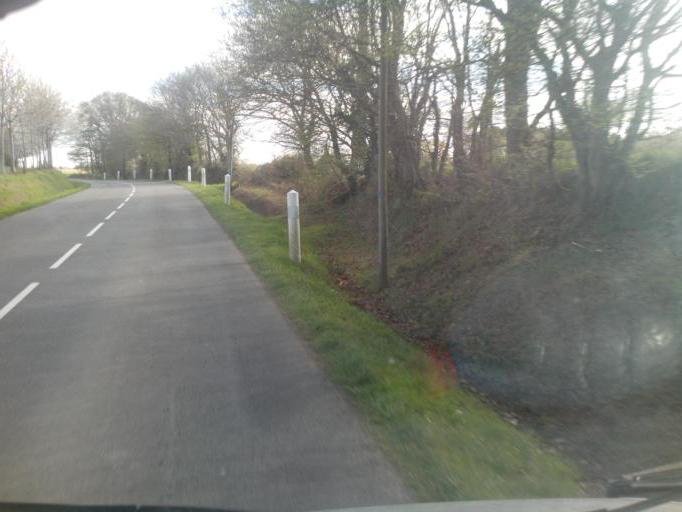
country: FR
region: Brittany
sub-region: Departement d'Ille-et-Vilaine
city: Paimpont
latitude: 48.0481
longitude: -2.1857
